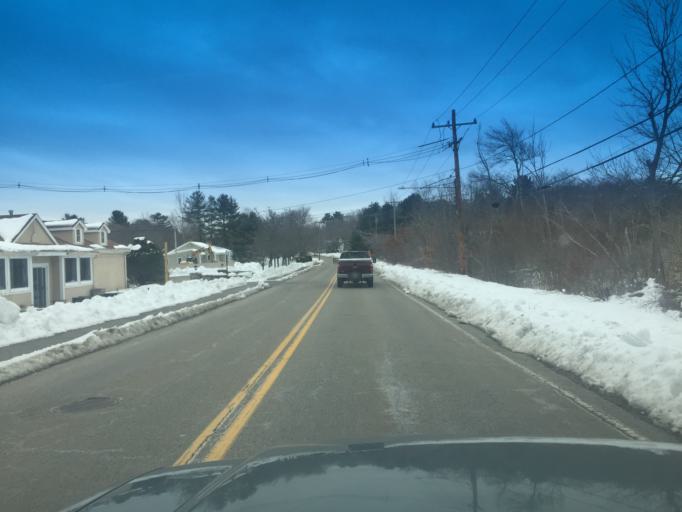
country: US
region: Massachusetts
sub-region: Norfolk County
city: Millis
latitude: 42.1626
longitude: -71.3661
